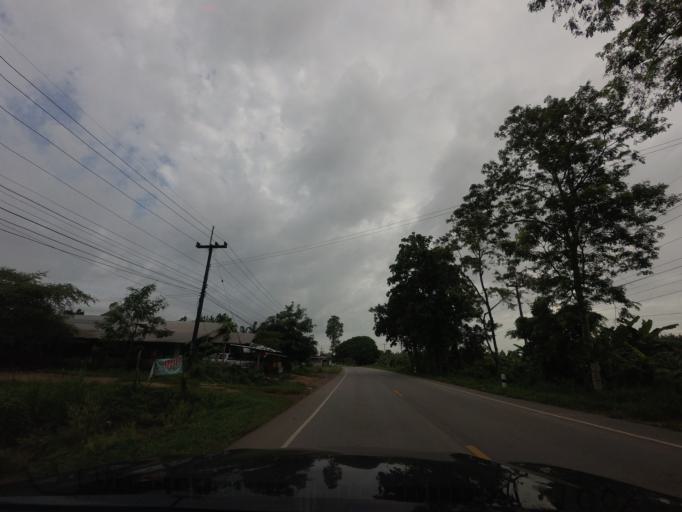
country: TH
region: Changwat Udon Thani
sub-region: Amphoe Ban Phue
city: Ban Phue
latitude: 17.7235
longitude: 102.3940
